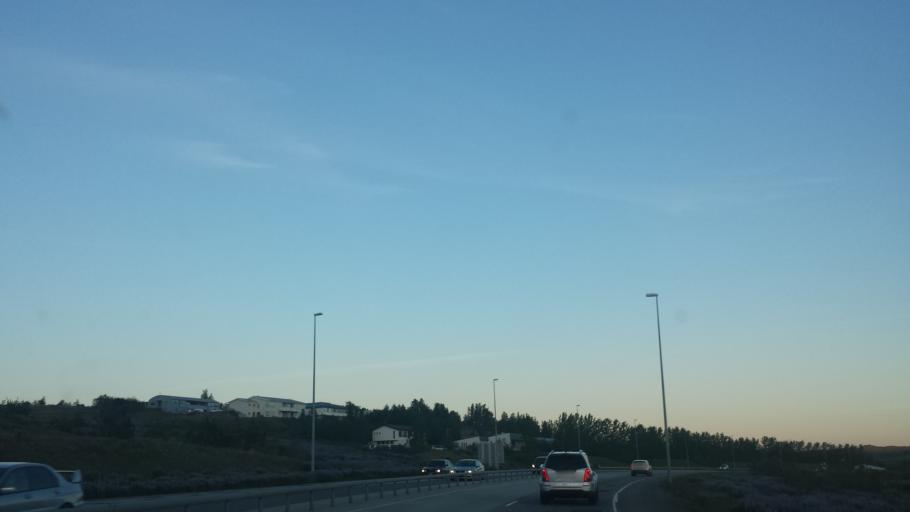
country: IS
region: Capital Region
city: Mosfellsbaer
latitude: 64.1753
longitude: -21.6769
